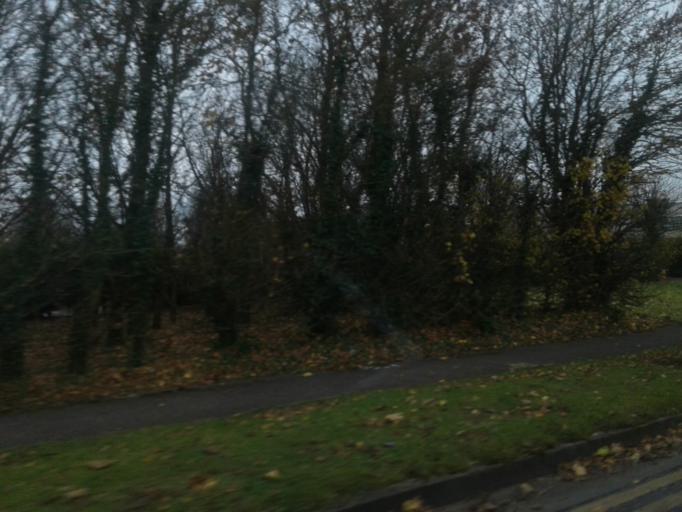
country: IE
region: Leinster
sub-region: Fingal County
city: Blanchardstown
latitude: 53.4068
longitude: -6.3561
